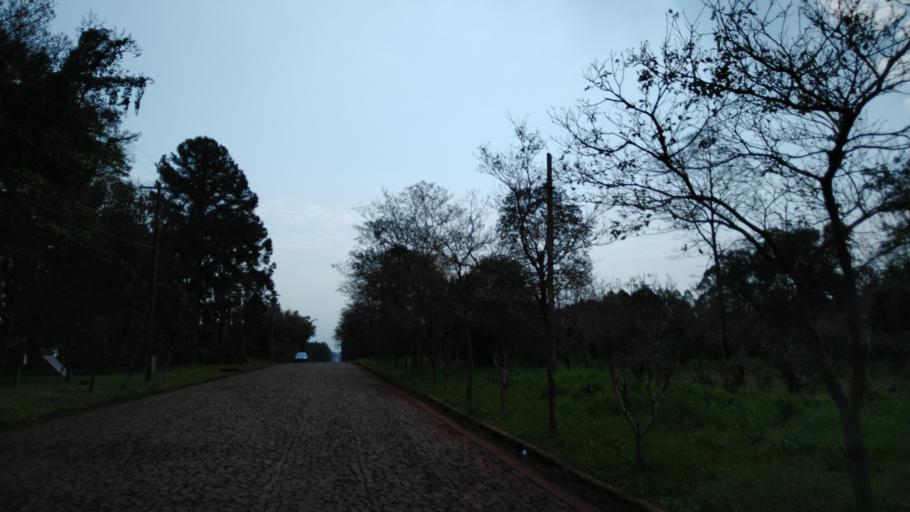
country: AR
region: Misiones
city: Capiovi
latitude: -26.9551
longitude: -55.0557
